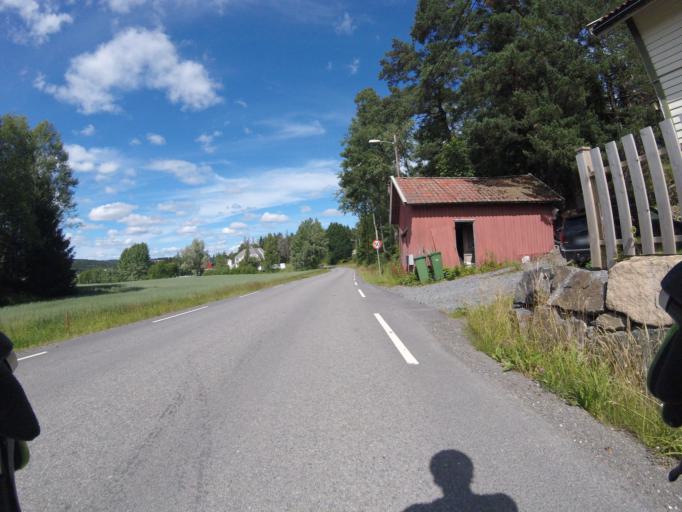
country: NO
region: Akershus
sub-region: Lorenskog
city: Kjenn
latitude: 59.8991
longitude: 10.9694
